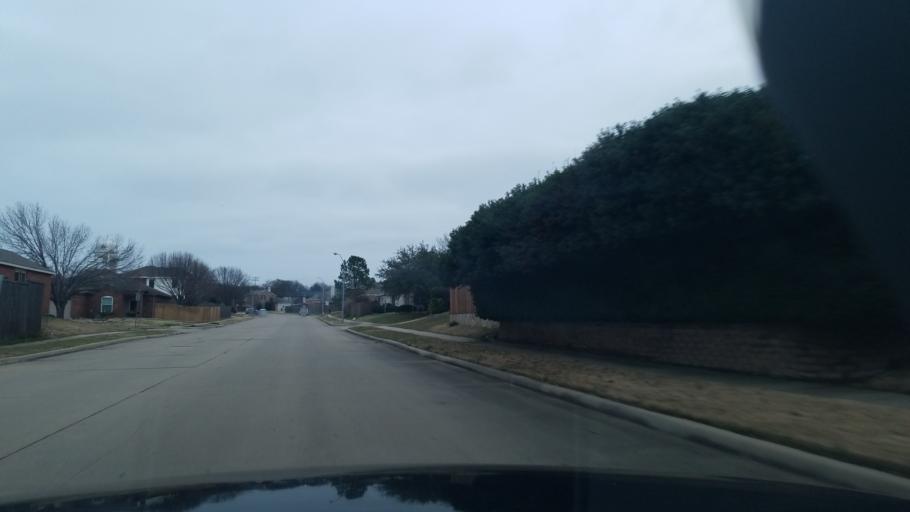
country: US
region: Texas
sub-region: Denton County
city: Corinth
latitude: 33.1368
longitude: -97.0691
